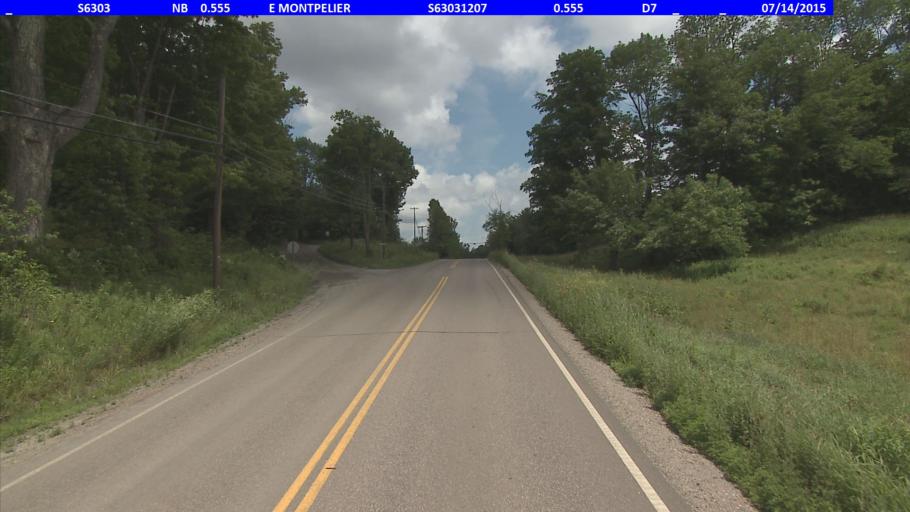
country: US
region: Vermont
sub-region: Washington County
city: Montpelier
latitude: 44.2792
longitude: -72.5512
